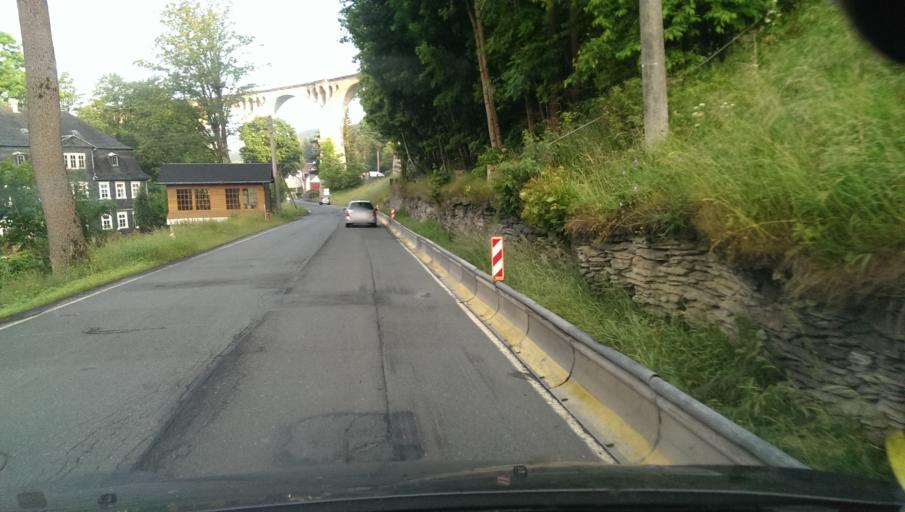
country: DE
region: Thuringia
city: Schmiedefeld
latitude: 50.5253
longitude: 11.2051
